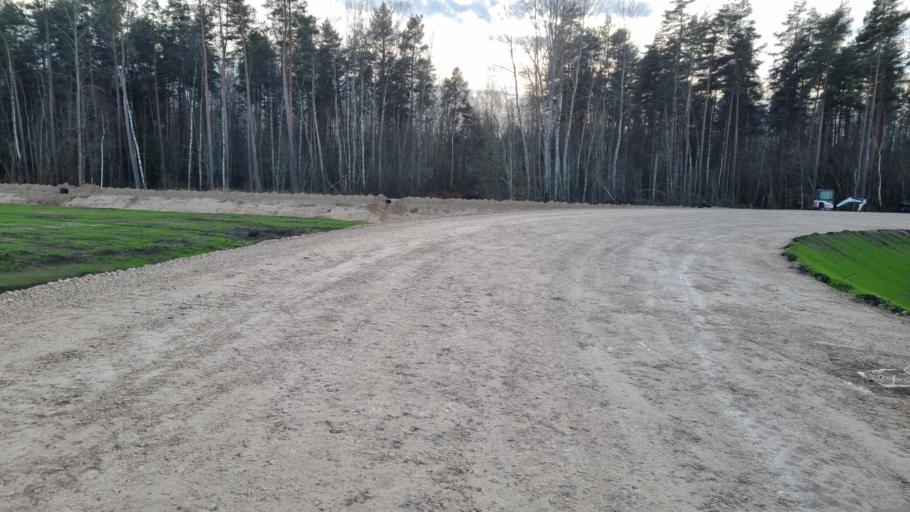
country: LV
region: Kekava
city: Kekava
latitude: 56.8074
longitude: 24.1966
